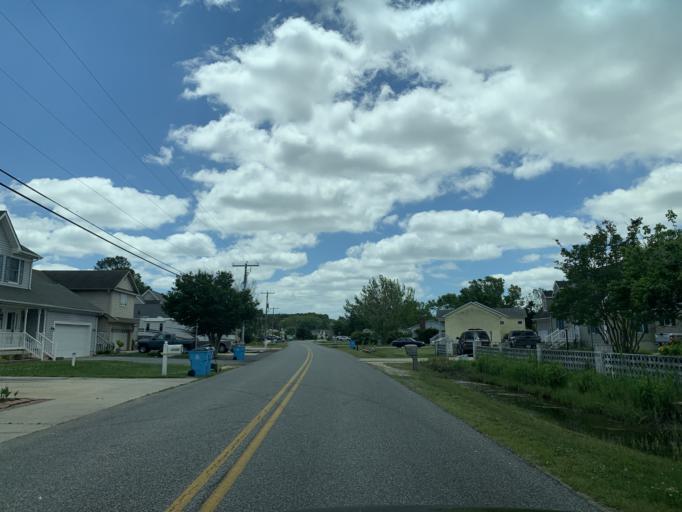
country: US
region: Maryland
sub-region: Worcester County
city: West Ocean City
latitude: 38.3553
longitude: -75.1194
